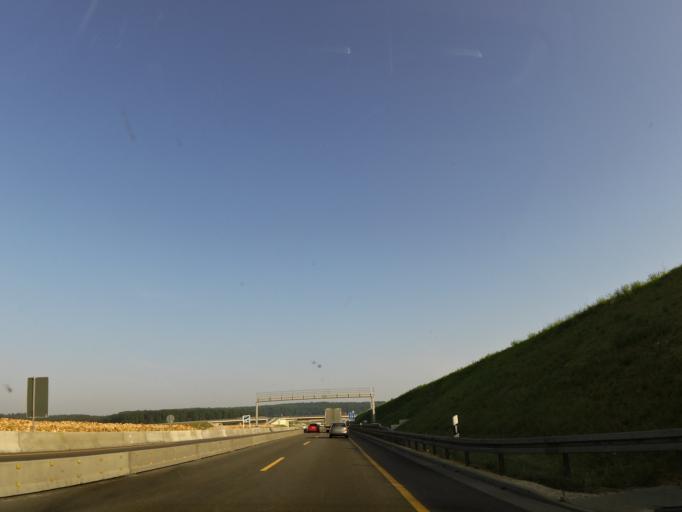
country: DE
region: Baden-Wuerttemberg
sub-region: Tuebingen Region
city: Lonsee
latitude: 48.4848
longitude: 9.8631
